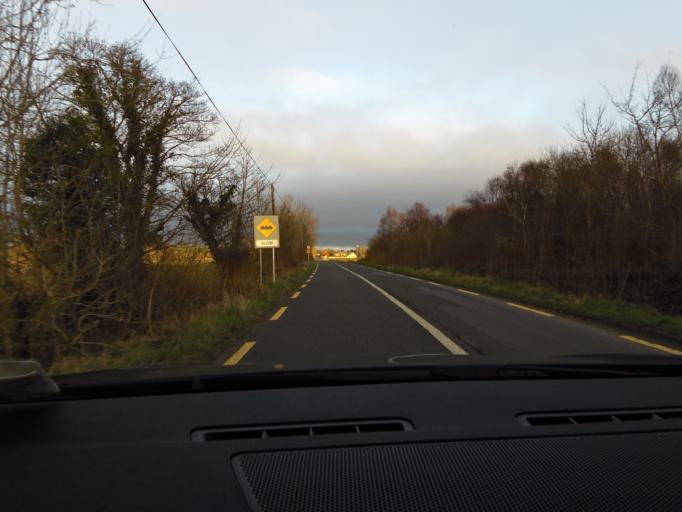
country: IE
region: Connaught
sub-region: Sligo
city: Ballymote
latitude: 54.0344
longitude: -8.6026
